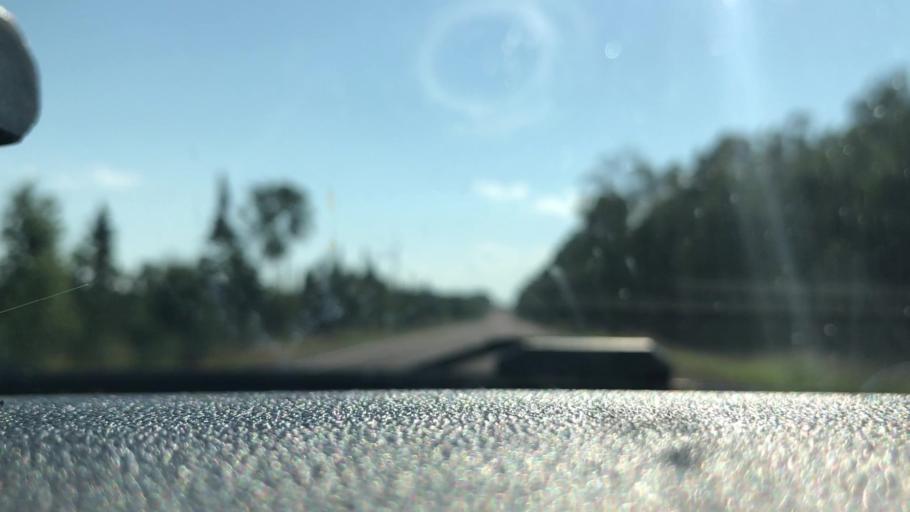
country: US
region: Minnesota
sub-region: Cook County
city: Grand Marais
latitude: 47.8312
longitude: -89.9803
